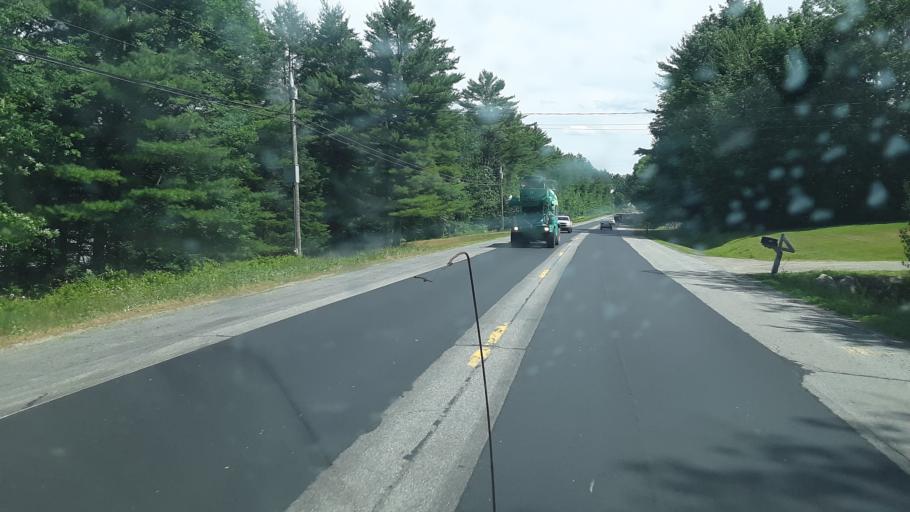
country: US
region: Maine
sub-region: Somerset County
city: Norridgewock
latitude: 44.6584
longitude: -69.7031
